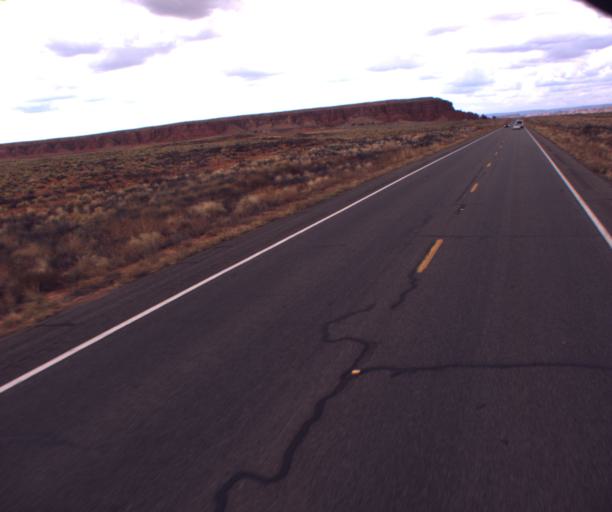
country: US
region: Arizona
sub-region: Navajo County
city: Kayenta
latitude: 36.7805
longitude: -109.9916
